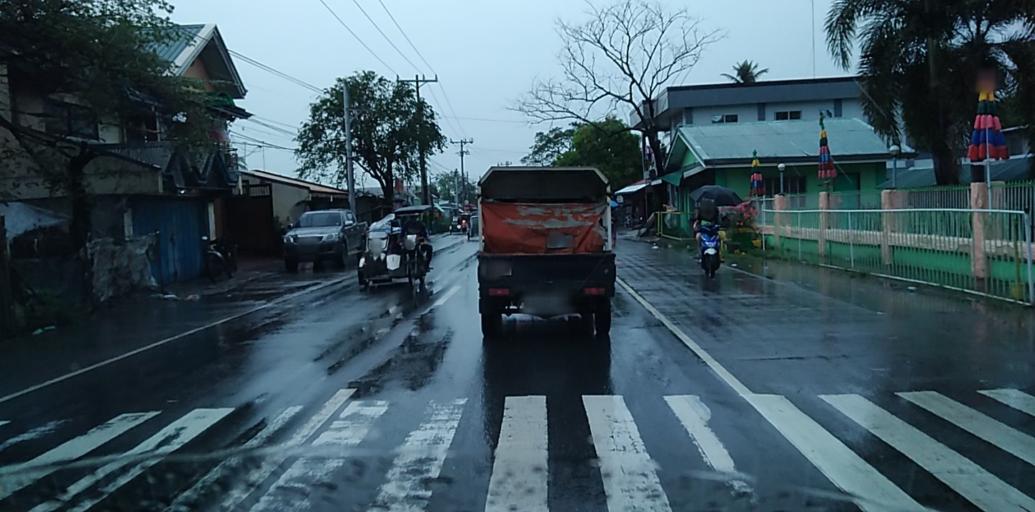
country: PH
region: Central Luzon
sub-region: Province of Bulacan
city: Bulualto
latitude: 15.2111
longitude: 120.9557
